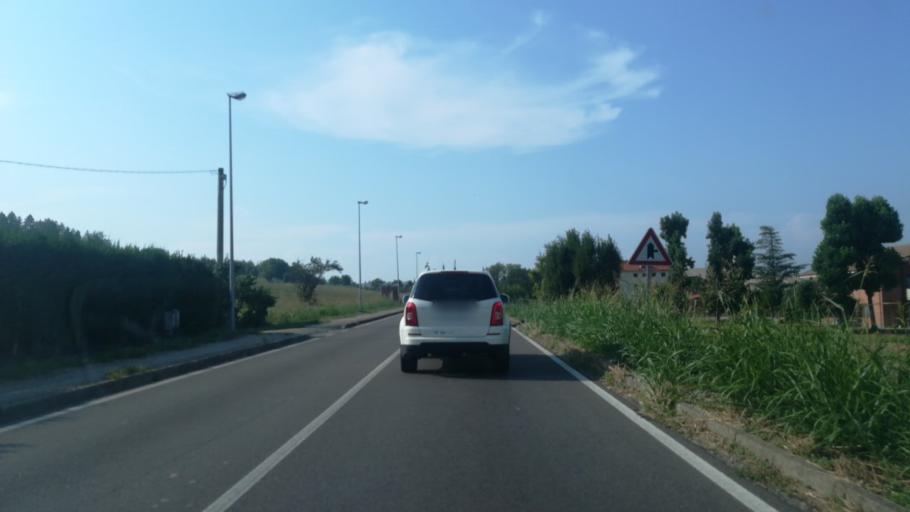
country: IT
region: Piedmont
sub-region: Provincia di Alessandria
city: Terruggia
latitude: 45.0927
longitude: 8.4617
